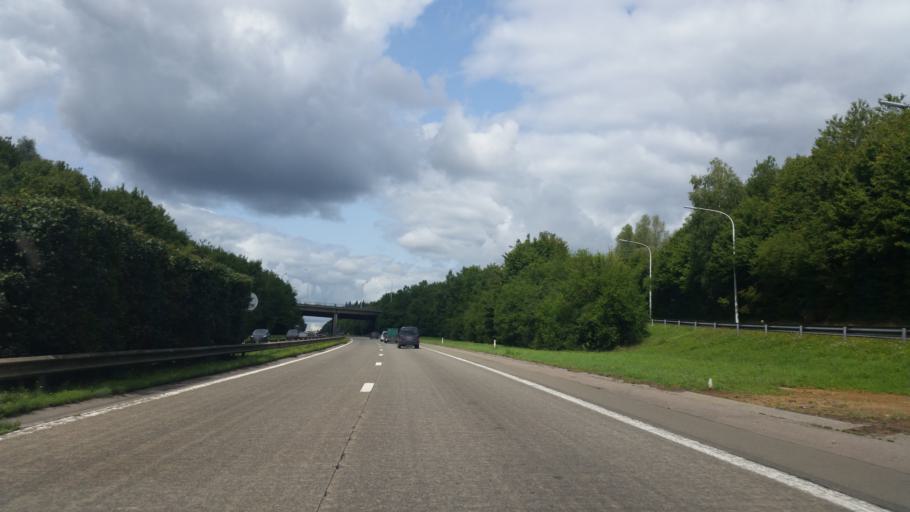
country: BE
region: Wallonia
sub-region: Province de Namur
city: Houyet
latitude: 50.2175
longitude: 5.0638
